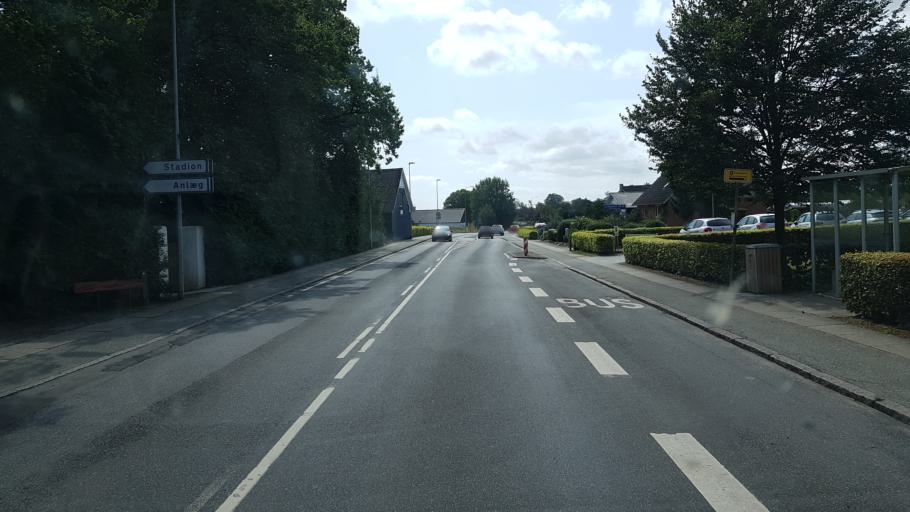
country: DK
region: South Denmark
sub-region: Vejen Kommune
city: Vejen
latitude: 55.5679
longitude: 9.1359
